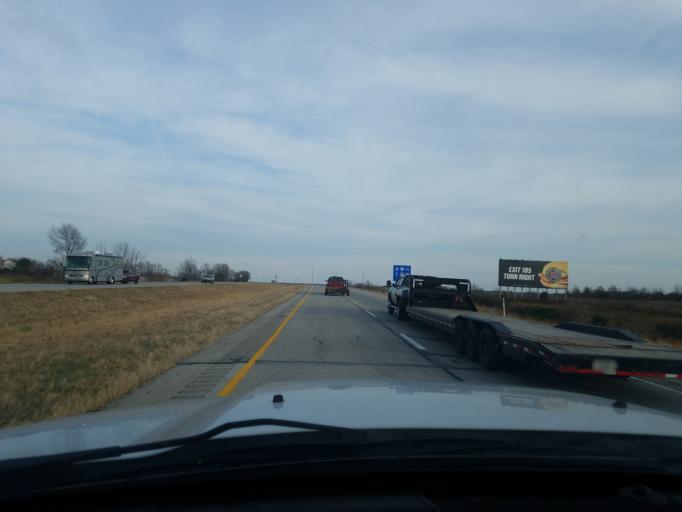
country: US
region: Indiana
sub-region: Harrison County
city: Corydon
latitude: 38.2391
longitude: -86.1403
